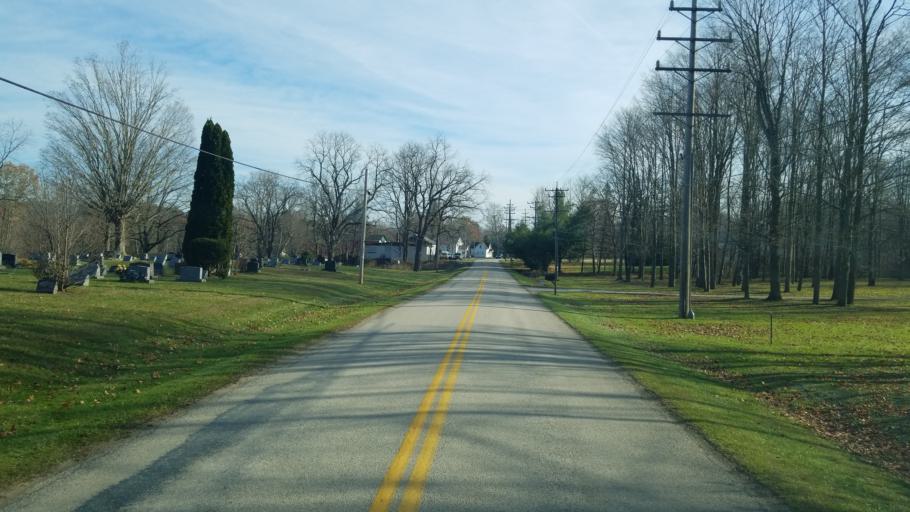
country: US
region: Ohio
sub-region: Ashtabula County
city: North Kingsville
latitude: 41.8449
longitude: -80.6675
